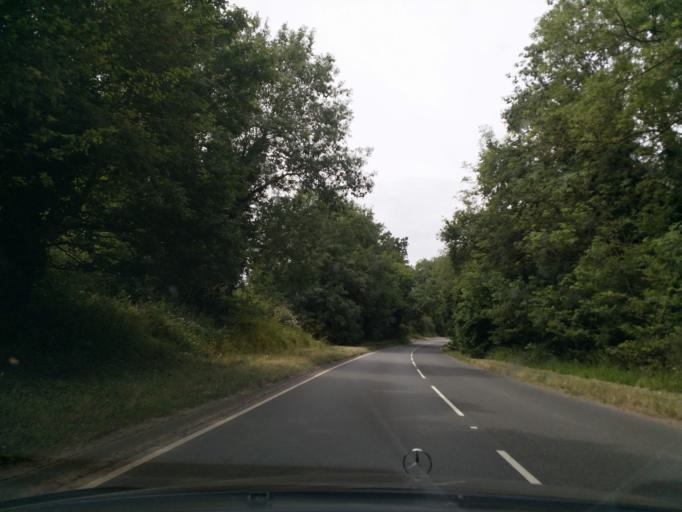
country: GB
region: England
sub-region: Solihull
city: Hampton in Arden
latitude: 52.4393
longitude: -1.6830
